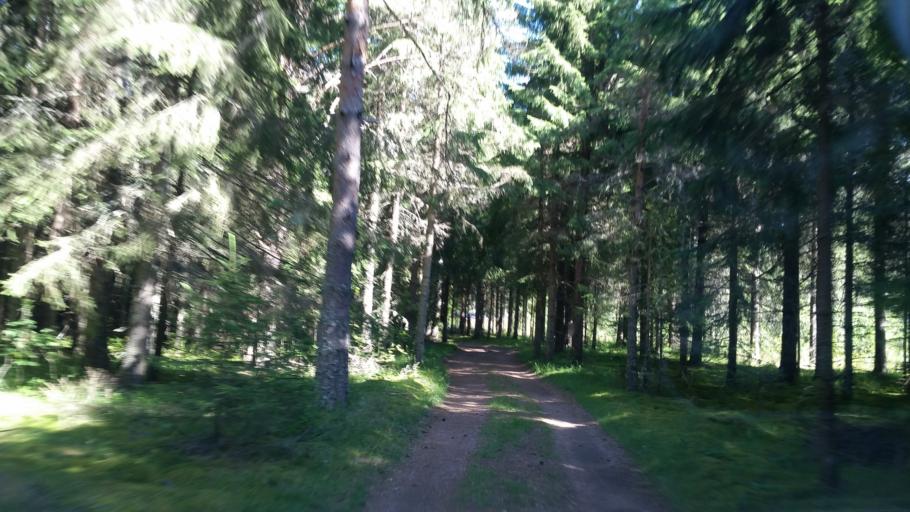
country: SE
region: Gaevleborg
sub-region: Ljusdals Kommun
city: Ljusdal
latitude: 61.9715
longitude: 16.3291
